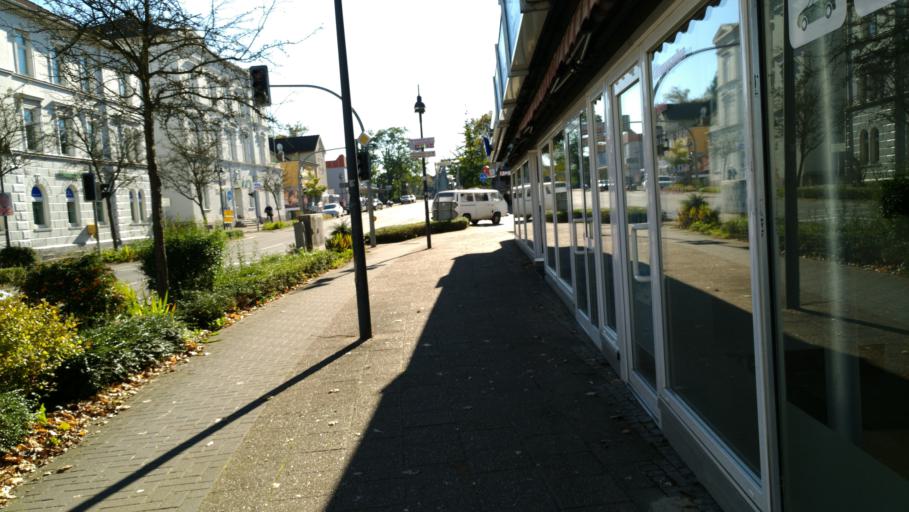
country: DE
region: Lower Saxony
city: Rinteln
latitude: 52.1925
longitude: 9.0818
